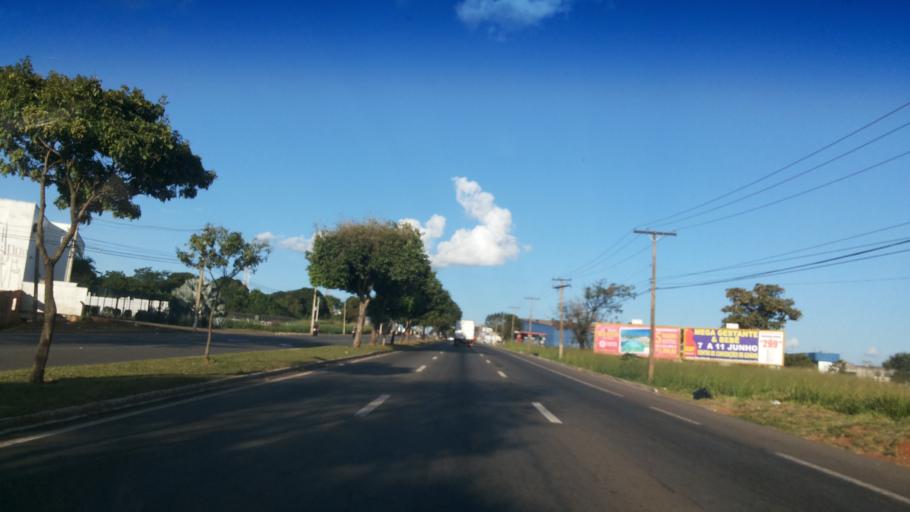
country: BR
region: Goias
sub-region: Goiania
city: Goiania
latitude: -16.6432
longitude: -49.2984
